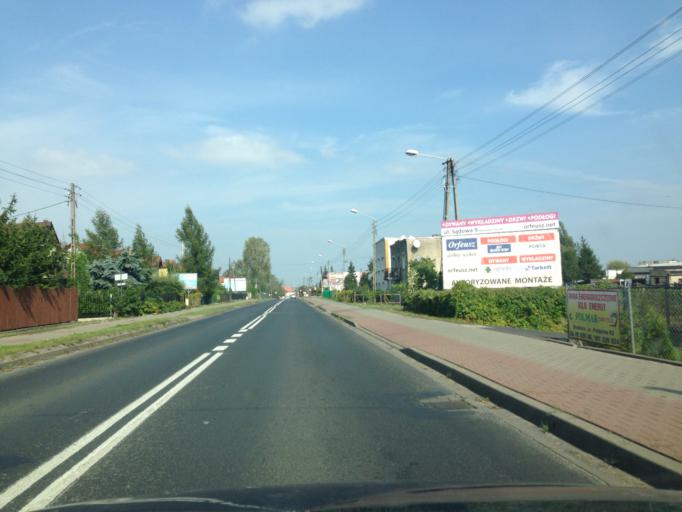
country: PL
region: Kujawsko-Pomorskie
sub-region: Powiat brodnicki
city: Brodnica
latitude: 53.2423
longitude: 19.3951
